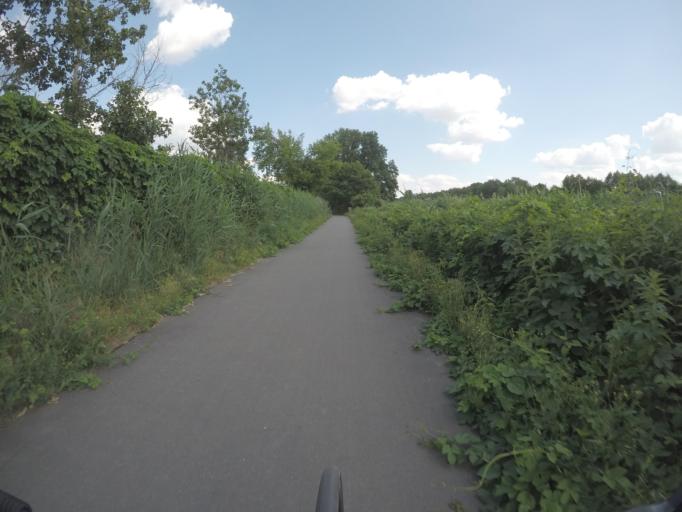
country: DE
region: Brandenburg
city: Roskow
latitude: 52.4526
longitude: 12.7809
